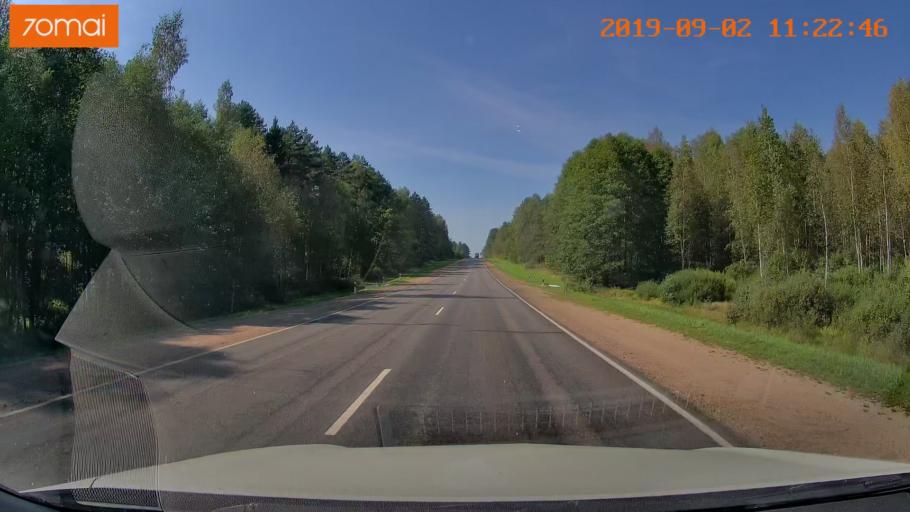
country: RU
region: Smolensk
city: Roslavl'
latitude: 54.0229
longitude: 33.0062
